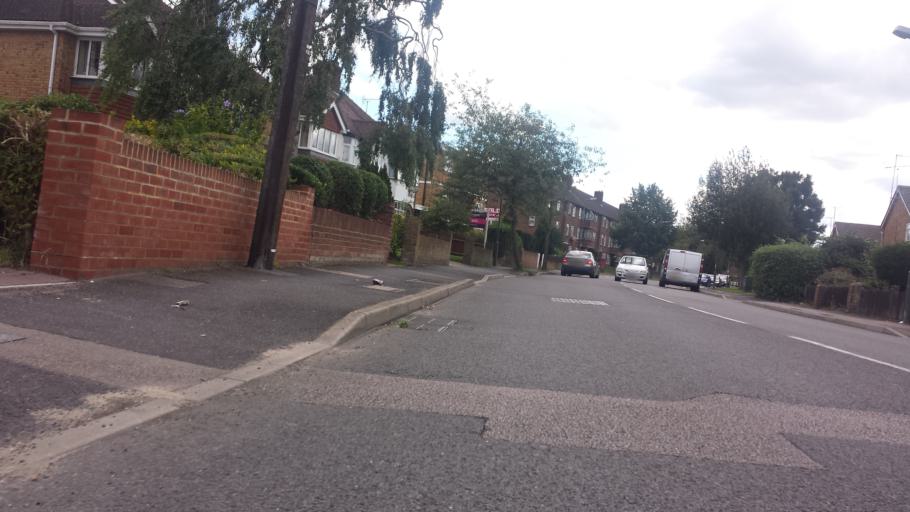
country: GB
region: England
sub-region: Greater London
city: Orpington
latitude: 51.3982
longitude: 0.1159
